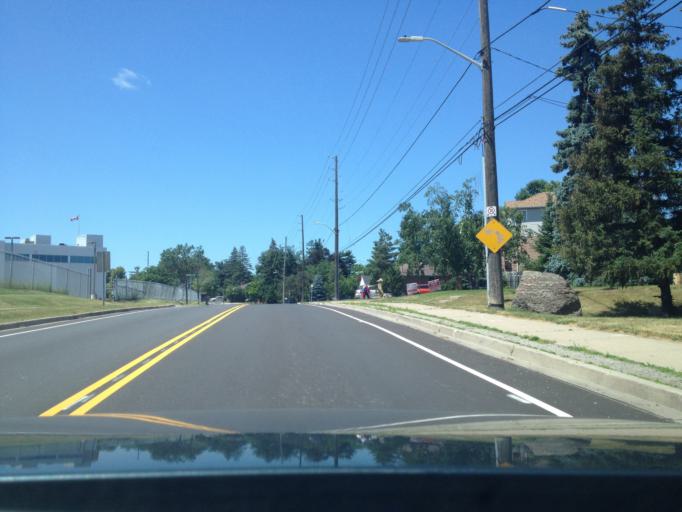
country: CA
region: Ontario
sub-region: Halton
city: Milton
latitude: 43.6605
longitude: -79.9111
